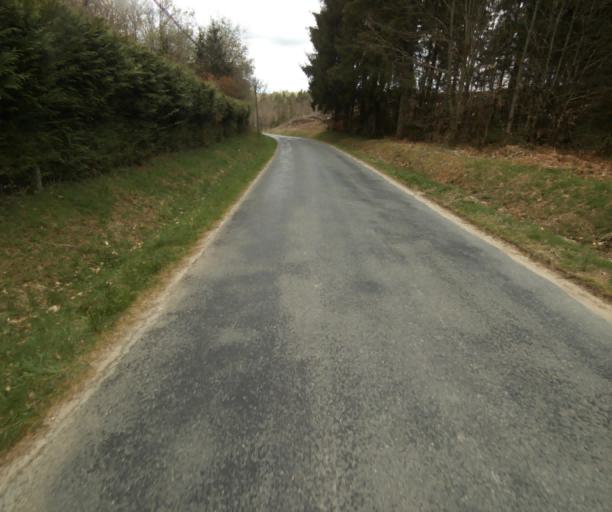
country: FR
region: Limousin
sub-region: Departement de la Correze
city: Correze
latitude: 45.3656
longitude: 1.9296
